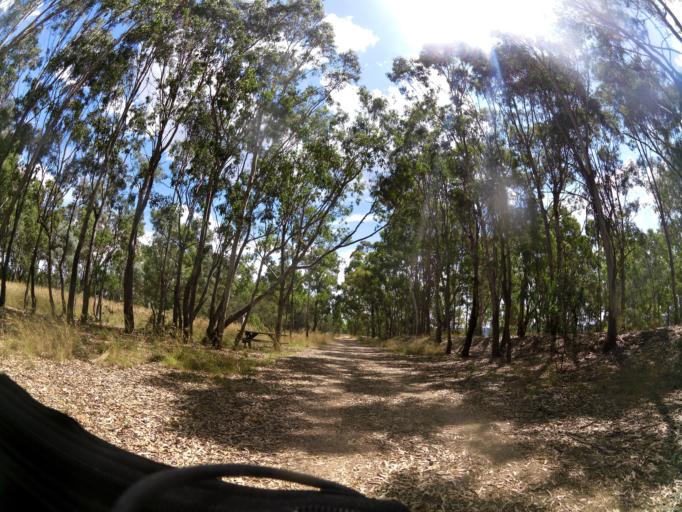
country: AU
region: Victoria
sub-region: Wellington
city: Heyfield
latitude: -37.9834
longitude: 146.7254
